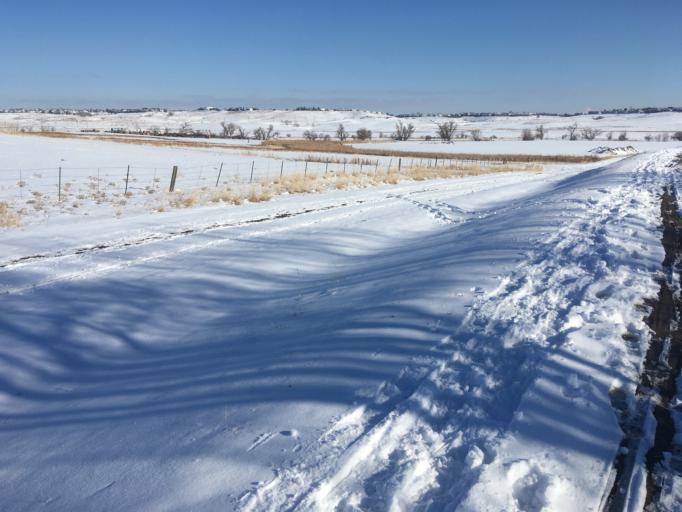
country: US
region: Colorado
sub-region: Broomfield County
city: Broomfield
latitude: 39.9492
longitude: -105.1040
